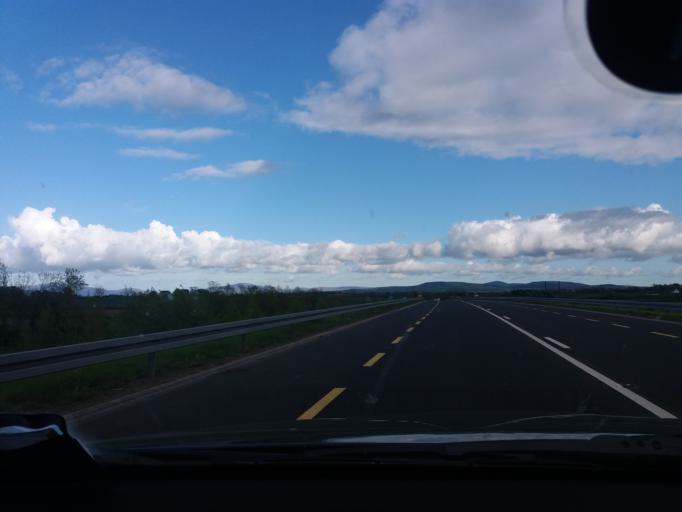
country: IE
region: Leinster
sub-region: Kilkenny
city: Kilkenny
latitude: 52.6403
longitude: -7.1686
